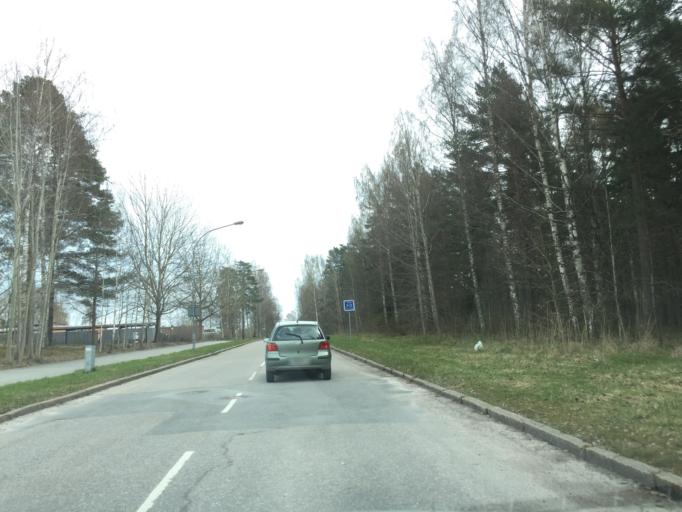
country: SE
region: OErebro
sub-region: Orebro Kommun
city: Orebro
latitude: 59.2948
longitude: 15.1888
